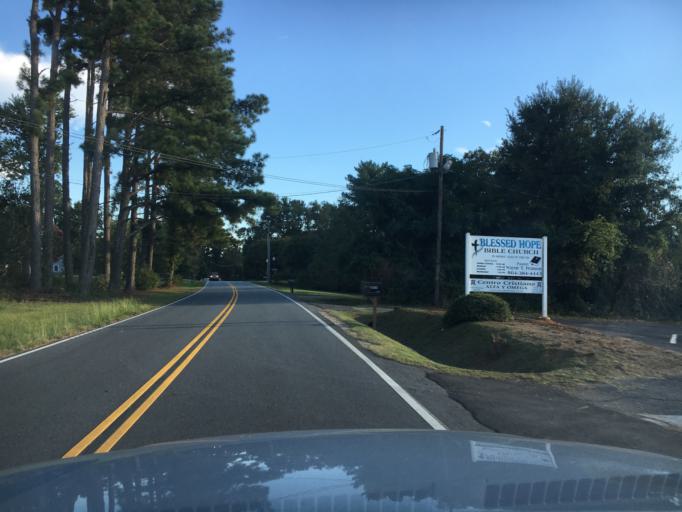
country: US
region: South Carolina
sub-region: Spartanburg County
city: Roebuck
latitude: 34.8976
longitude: -82.0074
